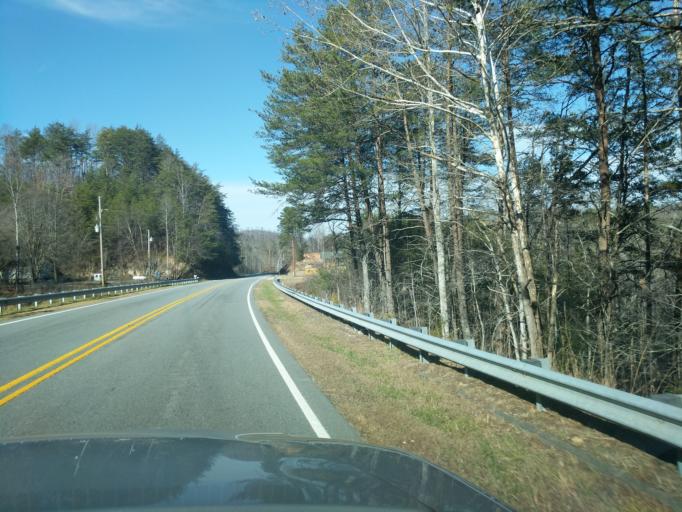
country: US
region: North Carolina
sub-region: McDowell County
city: West Marion
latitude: 35.5482
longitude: -81.9637
